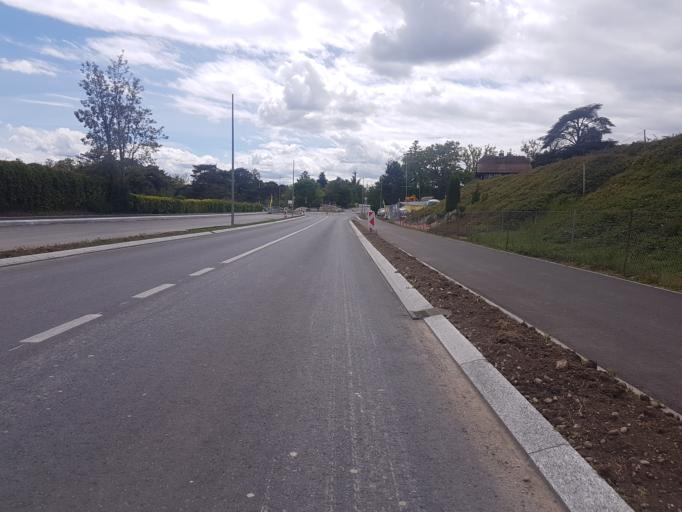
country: CH
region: Vaud
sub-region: Nyon District
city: Coppet
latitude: 46.3061
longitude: 6.1814
